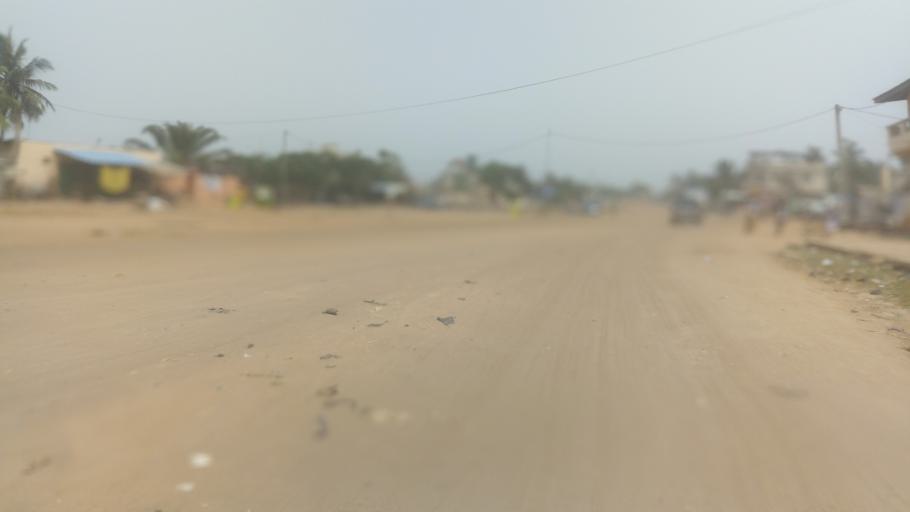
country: TG
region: Maritime
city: Lome
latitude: 6.1873
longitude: 1.1749
